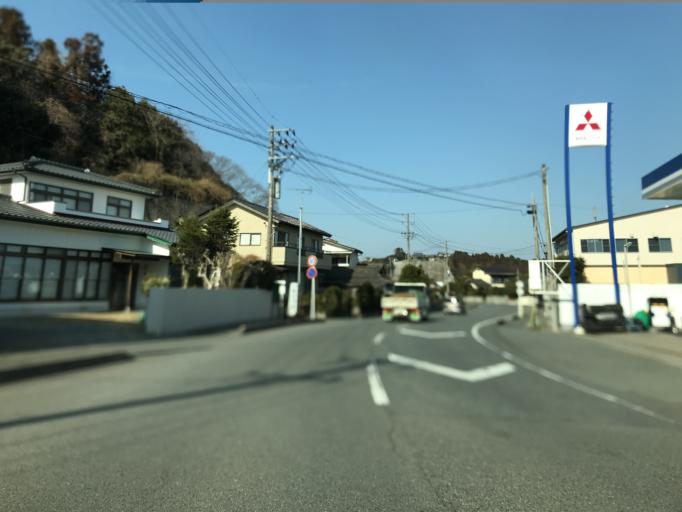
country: JP
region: Fukushima
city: Iwaki
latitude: 37.0350
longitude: 140.8525
